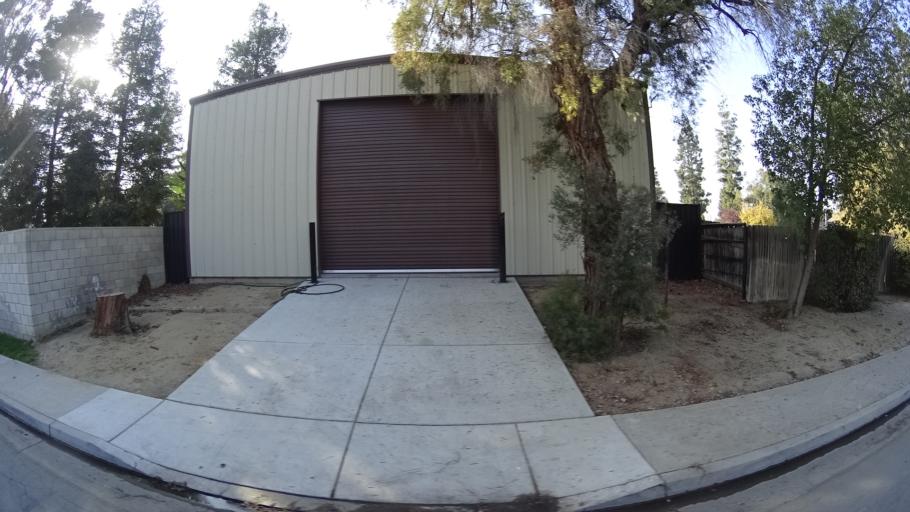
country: US
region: California
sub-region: Kern County
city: Rosedale
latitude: 35.3574
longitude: -119.1467
